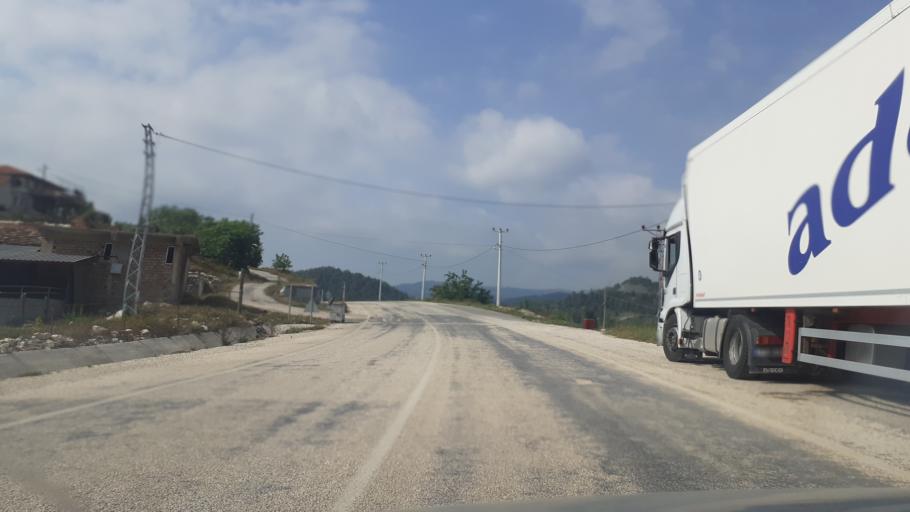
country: TR
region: Hatay
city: Yayladagi
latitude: 35.9103
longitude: 36.0541
